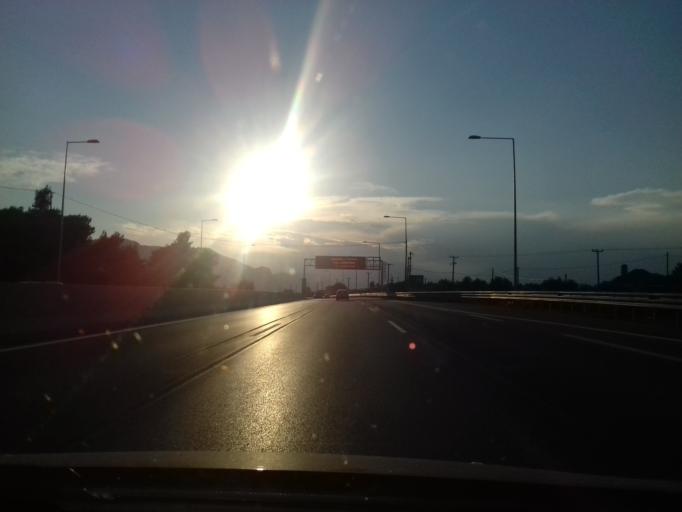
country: GR
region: West Greece
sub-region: Nomos Achaias
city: Akrata
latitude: 38.1712
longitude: 22.2967
